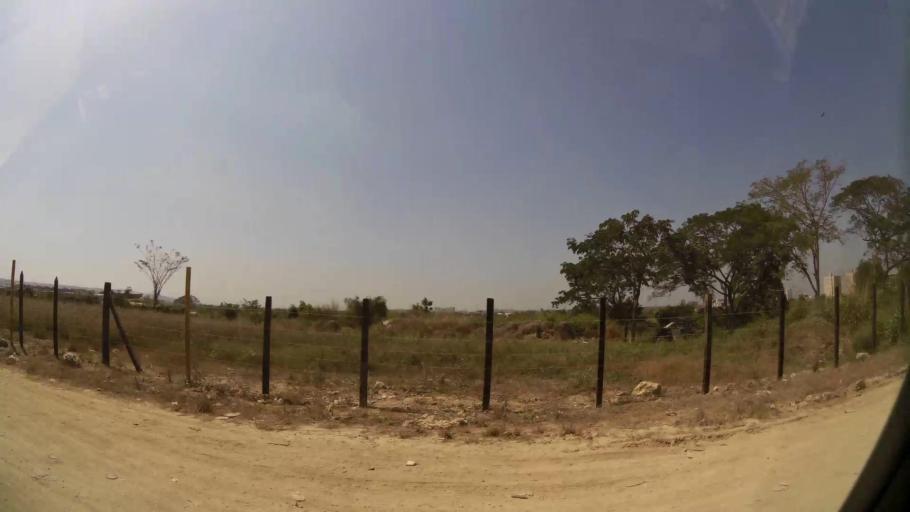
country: CO
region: Bolivar
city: Cartagena
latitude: 10.3959
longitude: -75.4514
